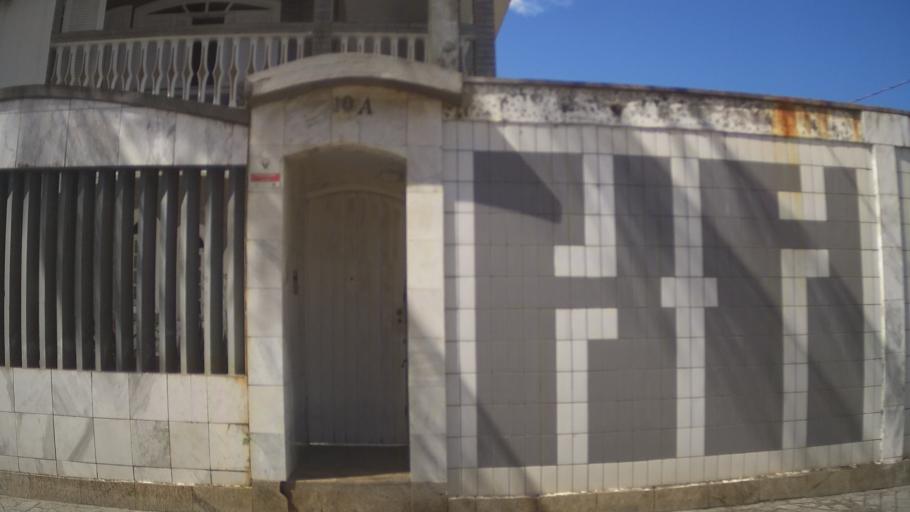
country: BR
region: Sao Paulo
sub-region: Itanhaem
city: Itanhaem
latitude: -24.1651
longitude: -46.7490
